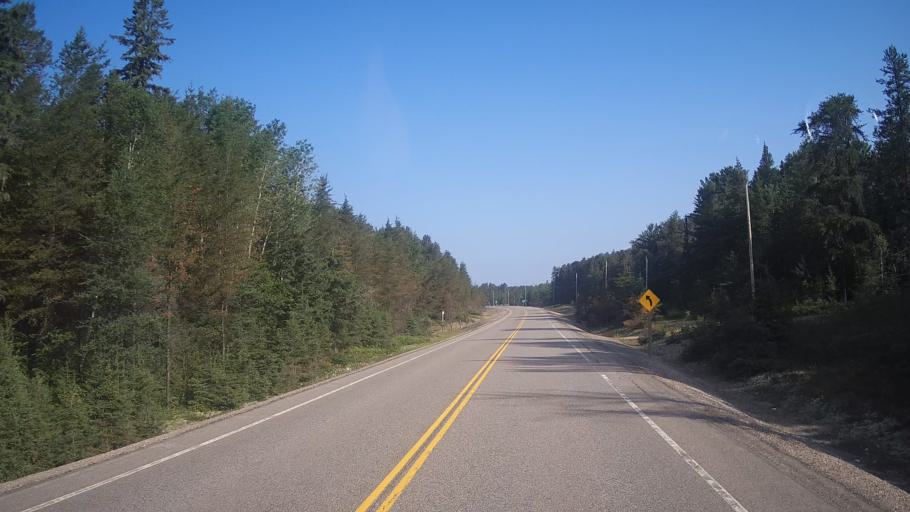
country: CA
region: Ontario
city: Rayside-Balfour
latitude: 46.7163
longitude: -81.5647
